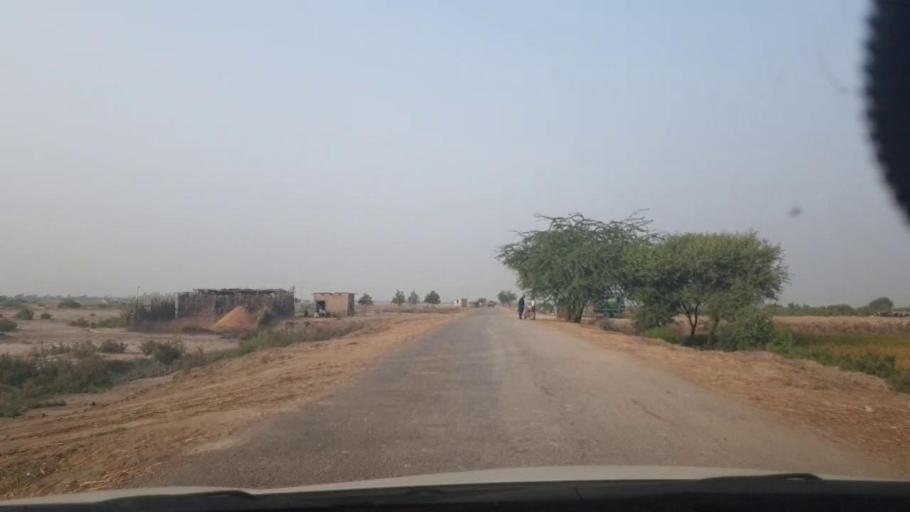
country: PK
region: Sindh
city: Bulri
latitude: 24.7847
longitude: 68.4194
